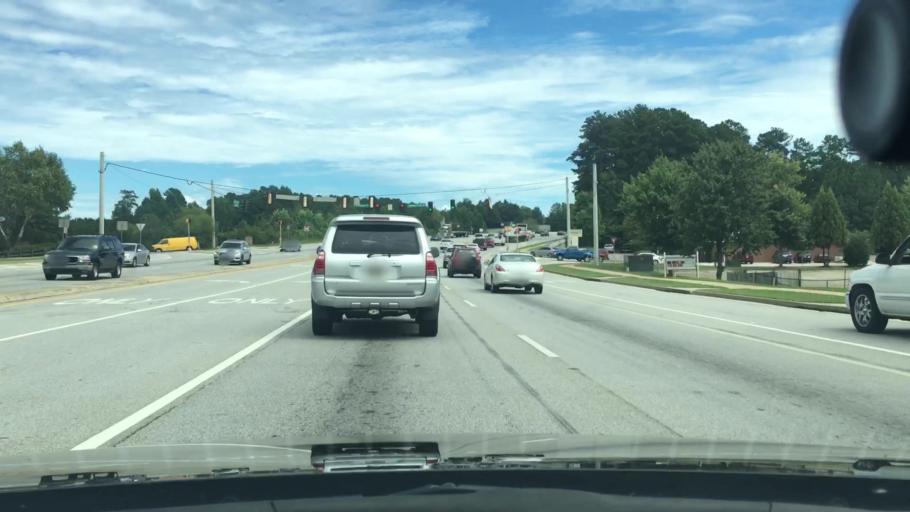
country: US
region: Georgia
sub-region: Coweta County
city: Newnan
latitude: 33.4006
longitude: -84.7714
